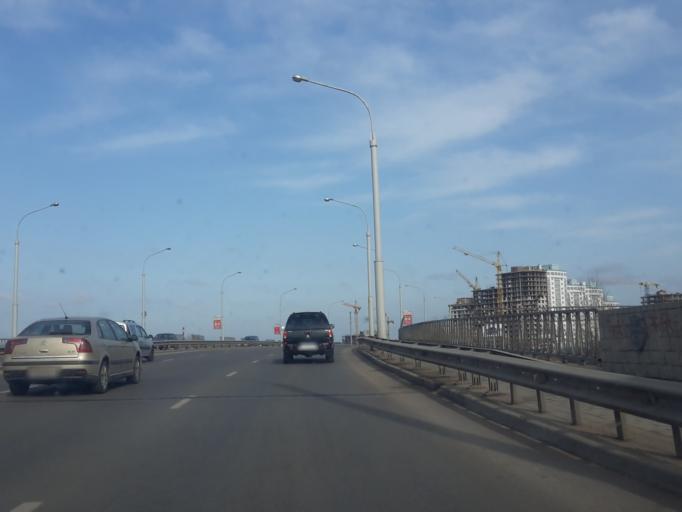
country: BY
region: Minsk
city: Minsk
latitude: 53.9083
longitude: 27.5240
